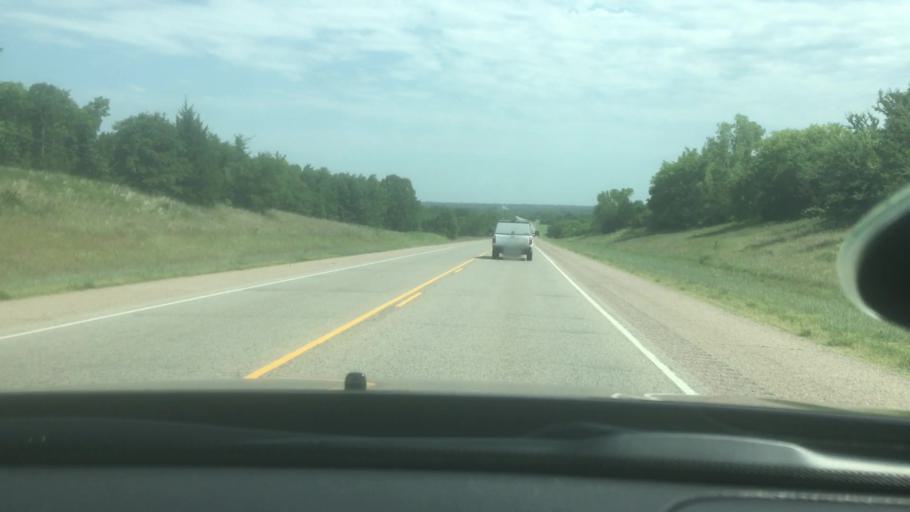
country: US
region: Oklahoma
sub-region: Seminole County
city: Maud
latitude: 35.0600
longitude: -96.9315
